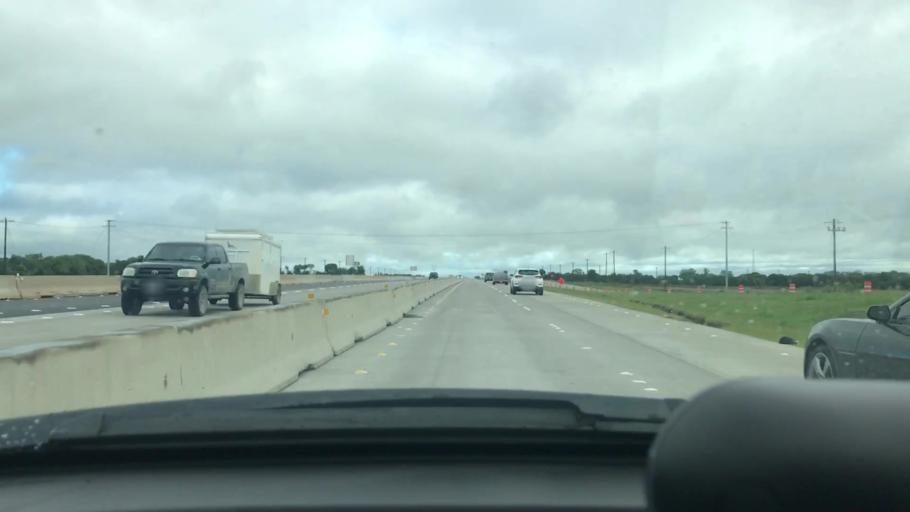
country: US
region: Texas
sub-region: Collin County
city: Anna
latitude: 33.3505
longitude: -96.5855
